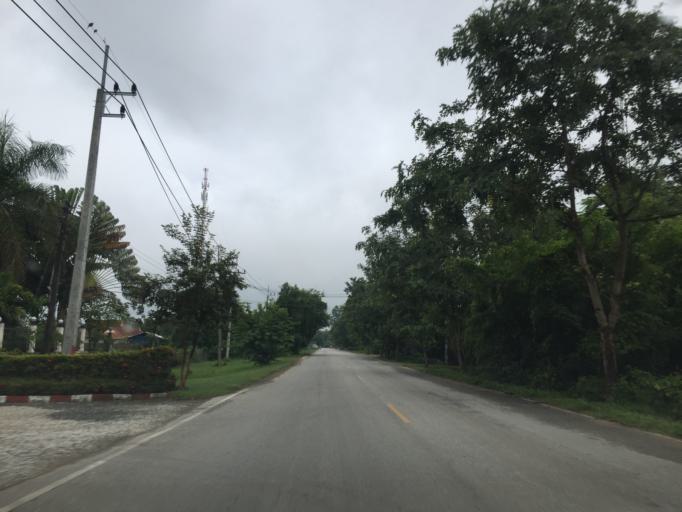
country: TH
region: Lamphun
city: Ban Thi
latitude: 18.6669
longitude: 99.0932
